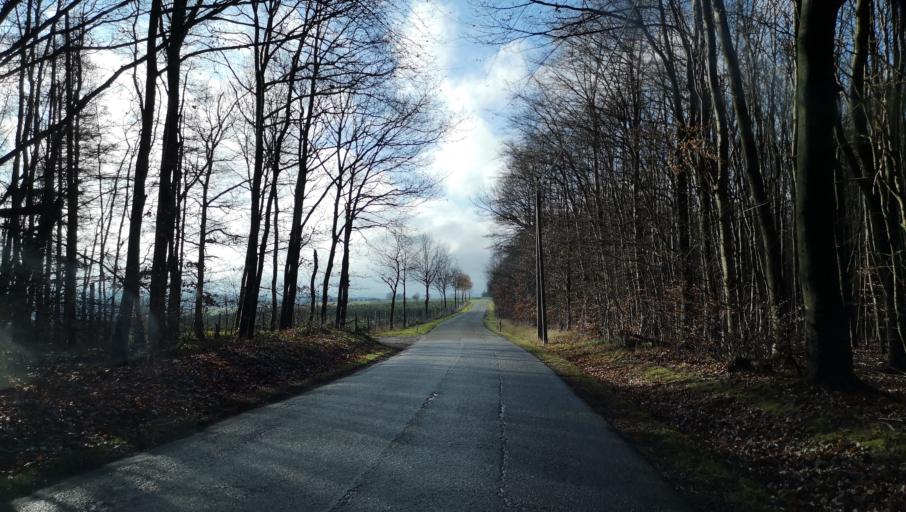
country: DE
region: North Rhine-Westphalia
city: Radevormwald
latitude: 51.2317
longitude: 7.3466
